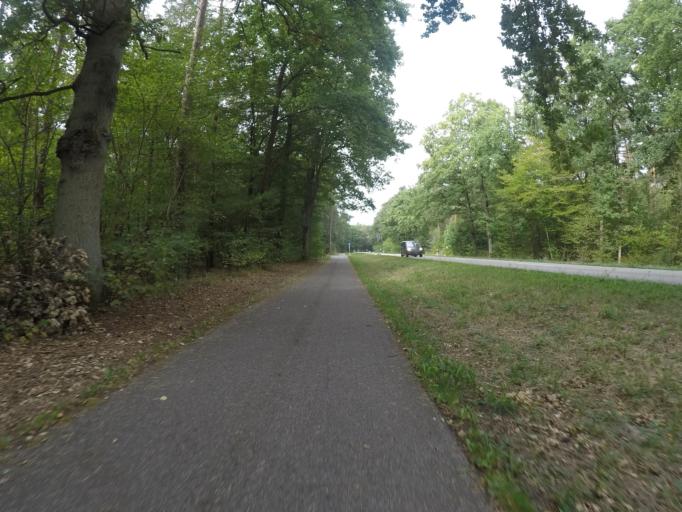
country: DE
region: Rheinland-Pfalz
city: Dudenhofen
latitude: 49.3460
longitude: 8.3649
